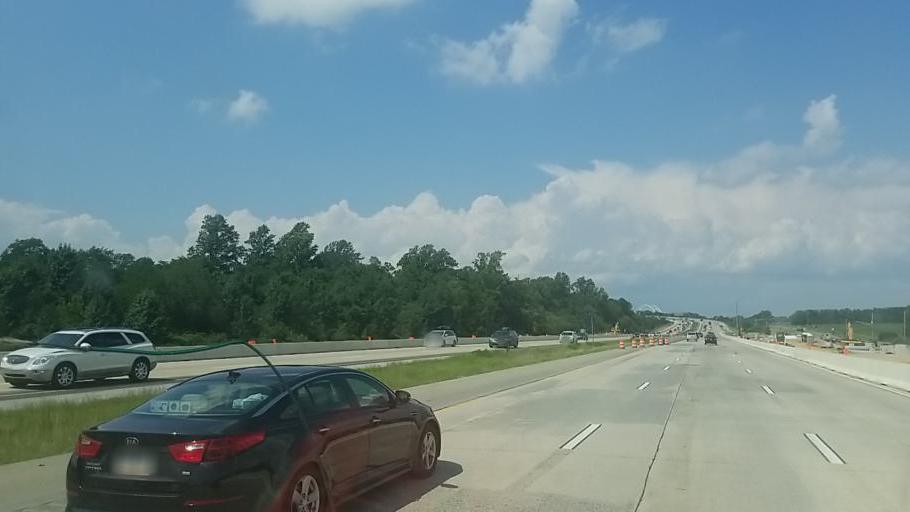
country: US
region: Delaware
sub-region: New Castle County
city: Delaware City
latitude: 39.5334
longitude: -75.6495
